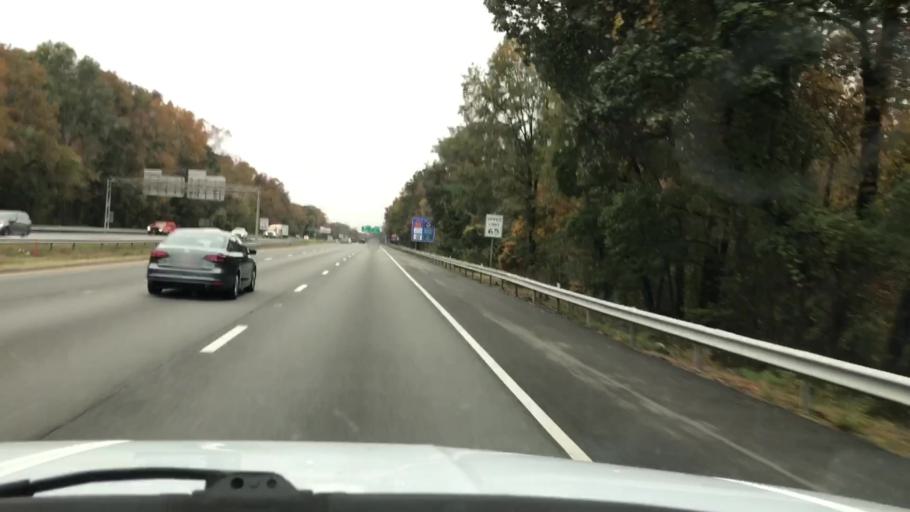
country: US
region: Virginia
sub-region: Henrico County
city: Chamberlayne
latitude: 37.6255
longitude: -77.4465
